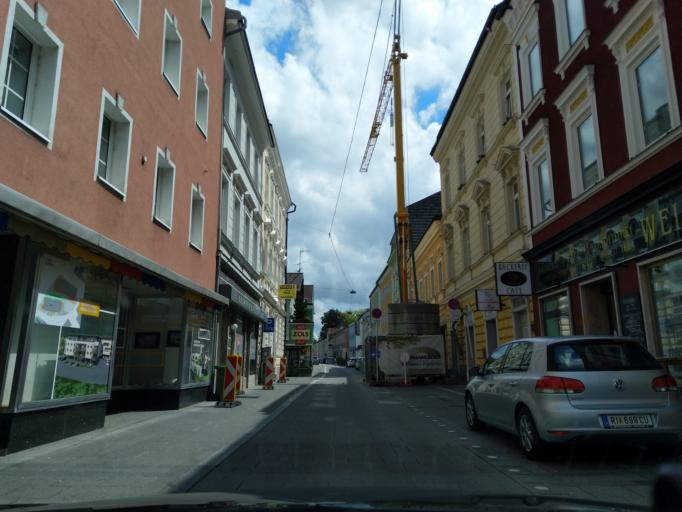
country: AT
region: Upper Austria
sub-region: Politischer Bezirk Ried im Innkreis
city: Ried im Innkreis
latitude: 48.2075
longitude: 13.4876
